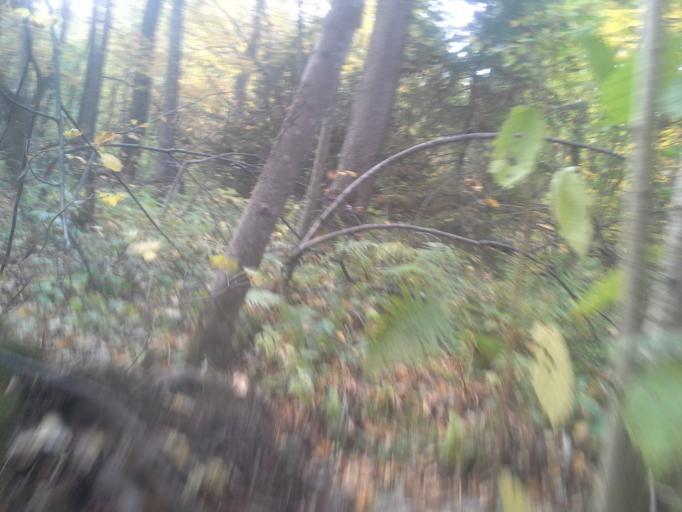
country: RU
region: Moskovskaya
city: Kievskij
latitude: 55.3856
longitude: 36.9186
